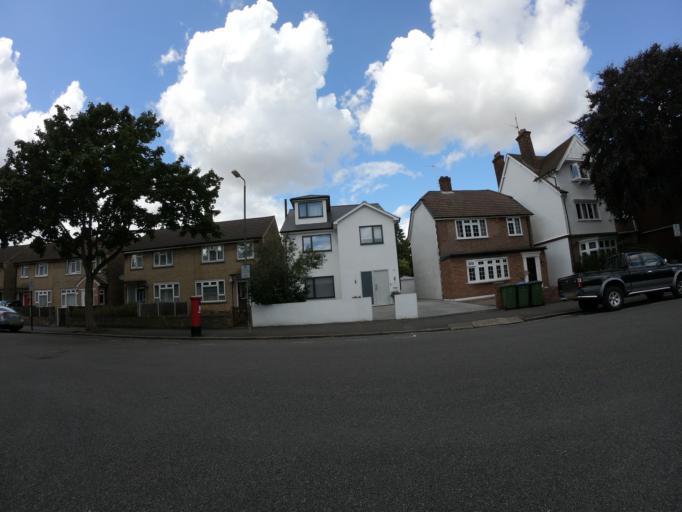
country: GB
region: England
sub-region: Greater London
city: Blackheath
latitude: 51.4810
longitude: 0.0140
